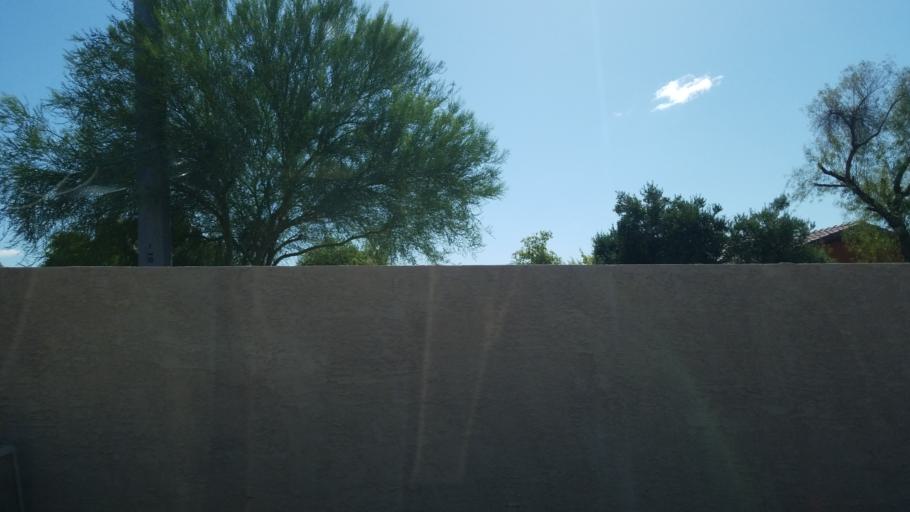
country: US
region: Arizona
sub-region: Maricopa County
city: Peoria
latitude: 33.6466
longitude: -112.2202
